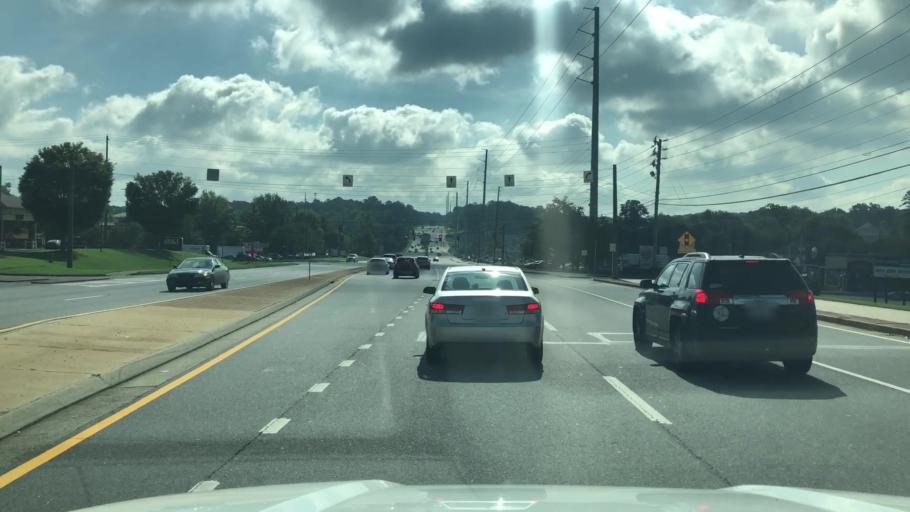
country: US
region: Georgia
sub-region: Cobb County
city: Marietta
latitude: 33.9462
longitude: -84.6259
